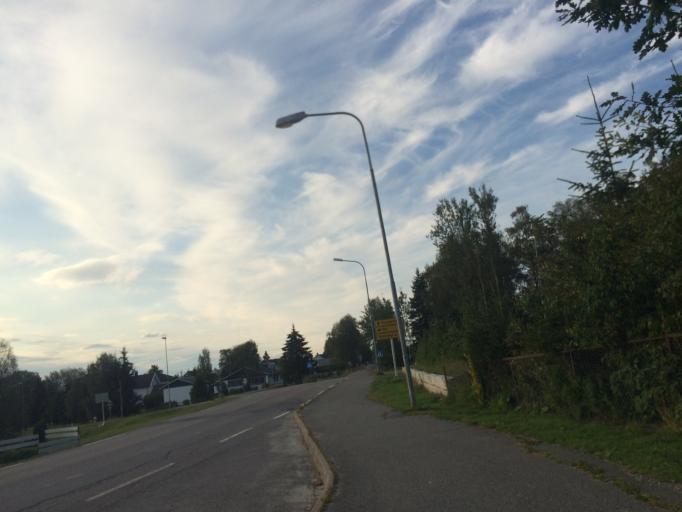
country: NO
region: Akershus
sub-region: Ski
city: Ski
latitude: 59.6807
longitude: 10.8839
